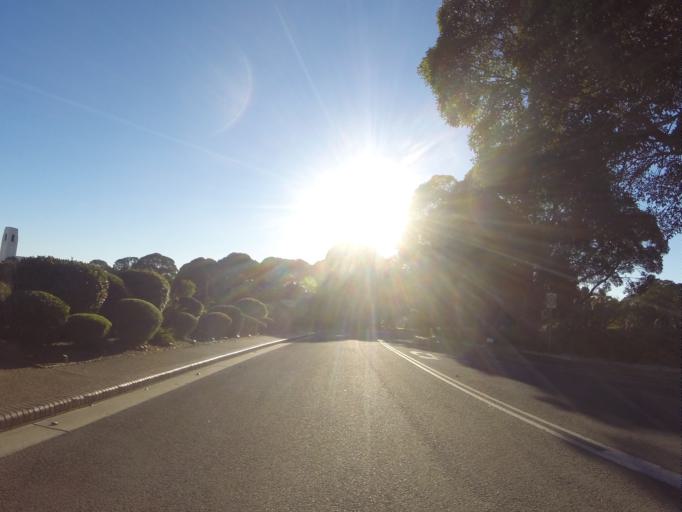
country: AU
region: New South Wales
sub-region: Sutherland Shire
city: Loftus
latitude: -34.0324
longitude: 151.0511
